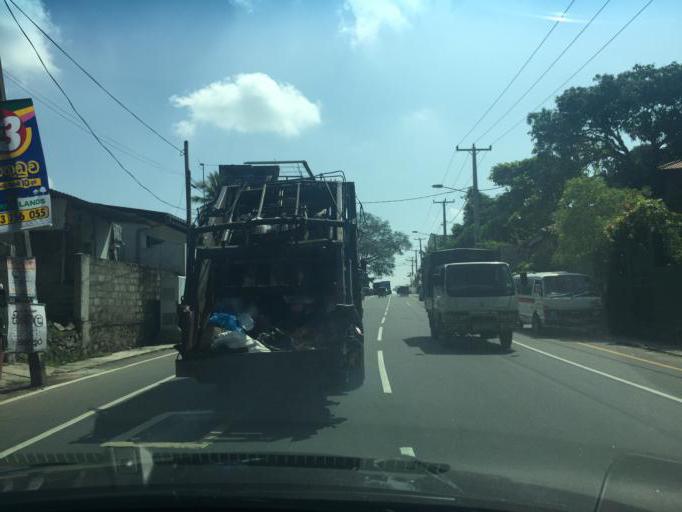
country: LK
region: Western
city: Sri Jayewardenepura Kotte
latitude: 6.8674
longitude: 79.8974
